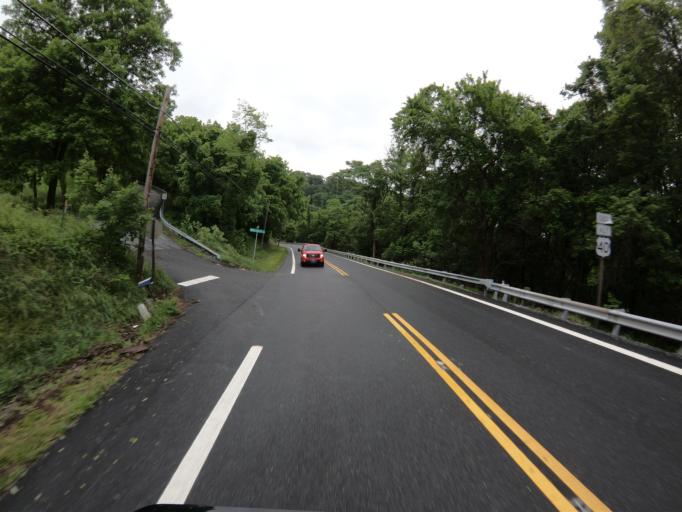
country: US
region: Maryland
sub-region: Washington County
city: Boonsboro
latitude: 39.4840
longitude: -77.6184
